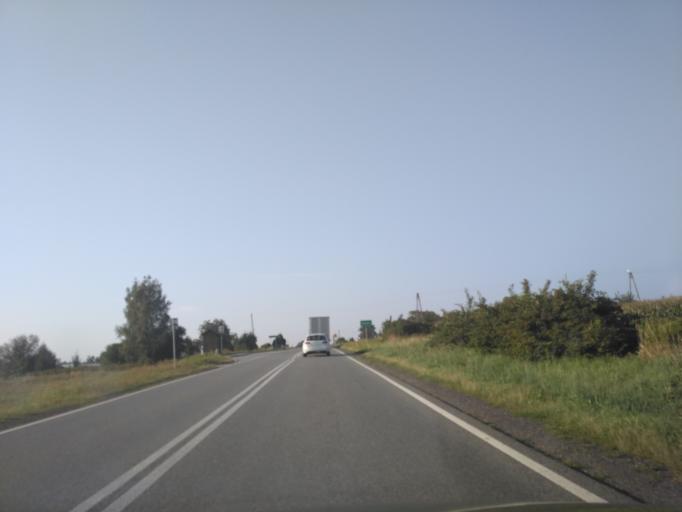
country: PL
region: Lublin Voivodeship
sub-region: Powiat janowski
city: Modliborzyce
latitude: 50.7970
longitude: 22.3184
